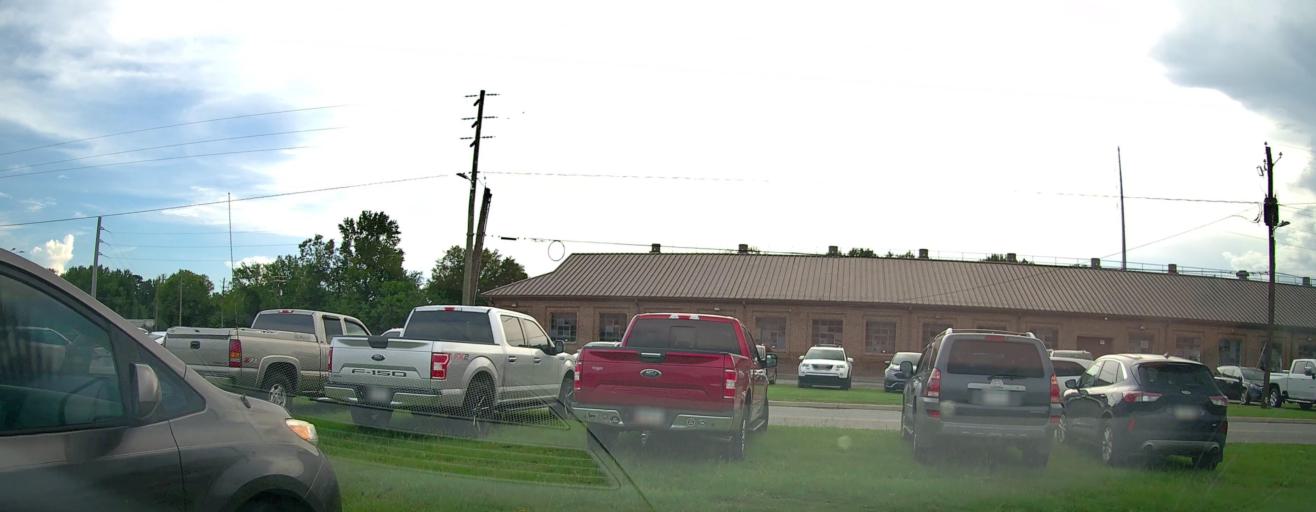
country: US
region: Georgia
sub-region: Bibb County
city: Macon
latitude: 32.8300
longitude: -83.6163
